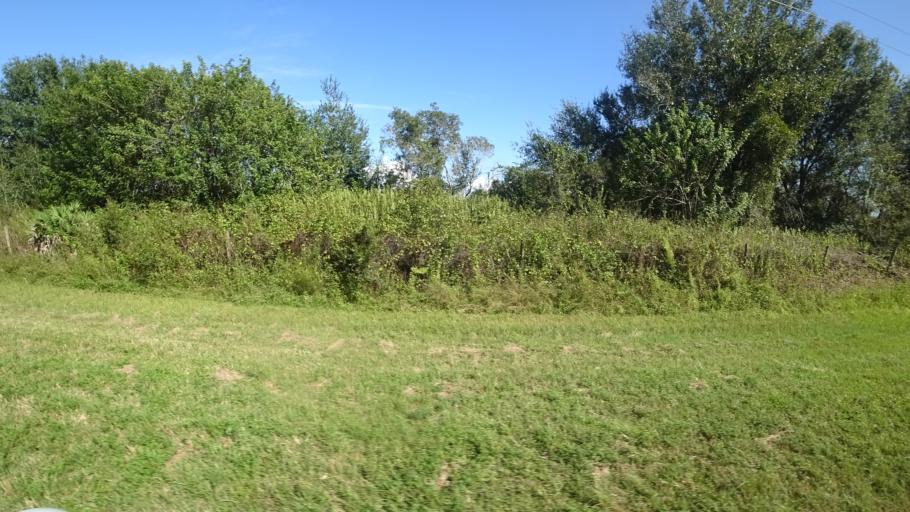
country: US
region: Florida
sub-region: Sarasota County
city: The Meadows
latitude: 27.4311
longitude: -82.2707
